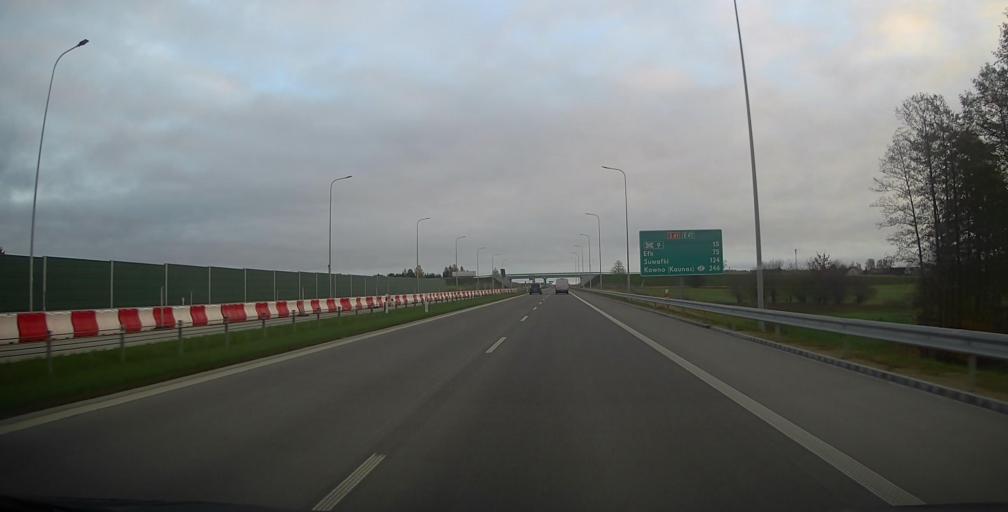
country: PL
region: Podlasie
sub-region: Powiat lomzynski
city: Piatnica
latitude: 53.2532
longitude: 22.1090
